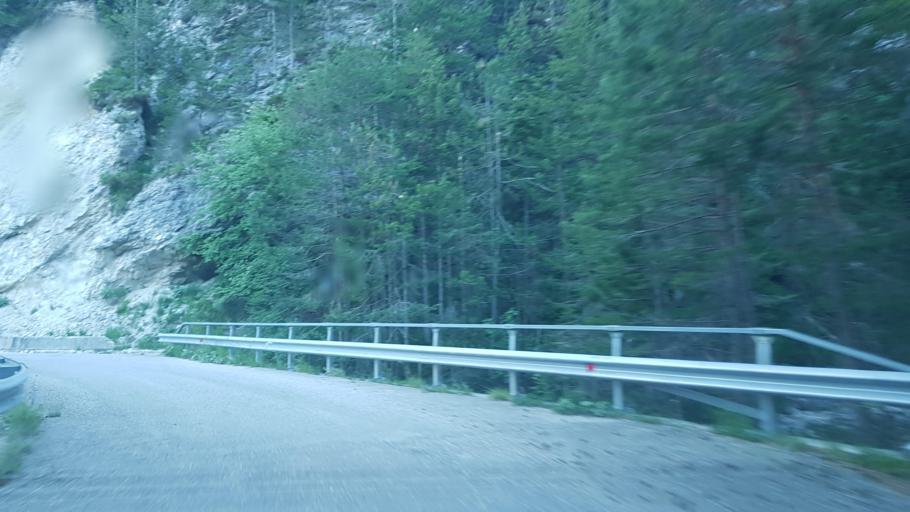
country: IT
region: Friuli Venezia Giulia
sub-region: Provincia di Udine
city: Malborghetto
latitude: 46.4609
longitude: 13.3910
